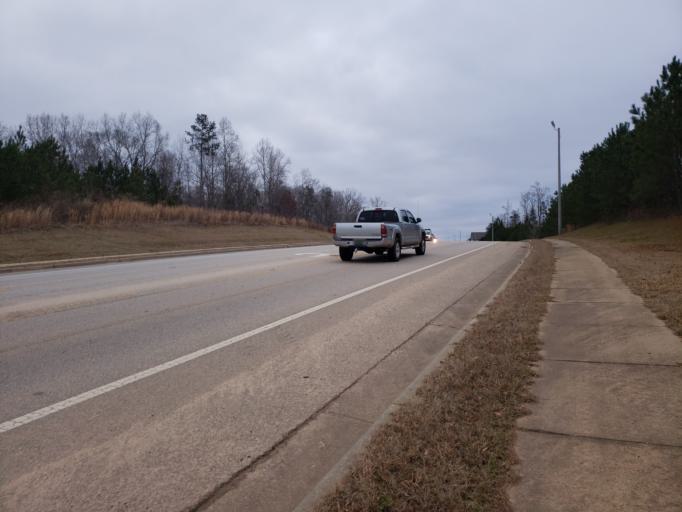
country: US
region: Alabama
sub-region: Lee County
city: Auburn
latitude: 32.5994
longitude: -85.4463
